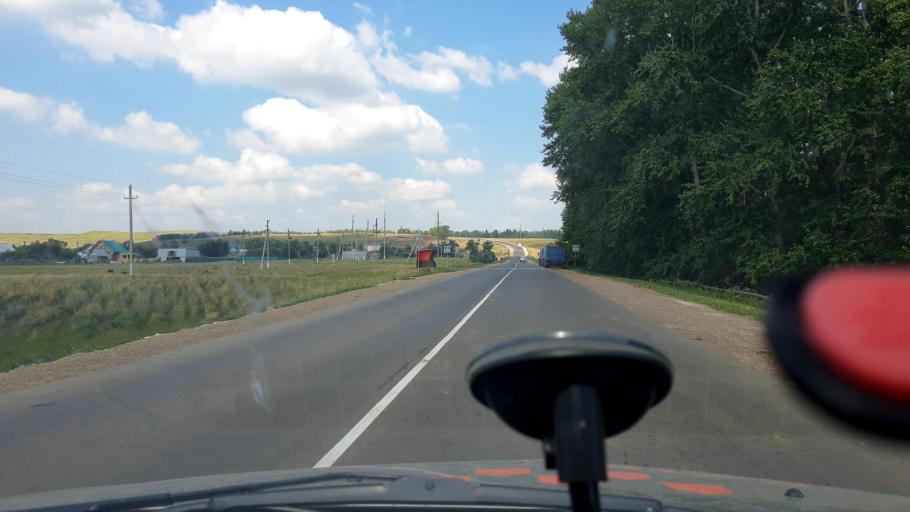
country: RU
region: Bashkortostan
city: Chekmagush
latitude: 54.8988
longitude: 54.5837
